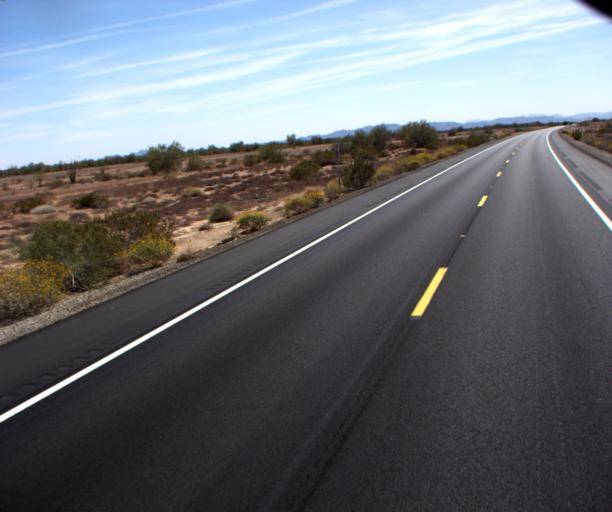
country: US
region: Arizona
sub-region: Yuma County
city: Wellton
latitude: 33.0056
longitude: -114.2852
